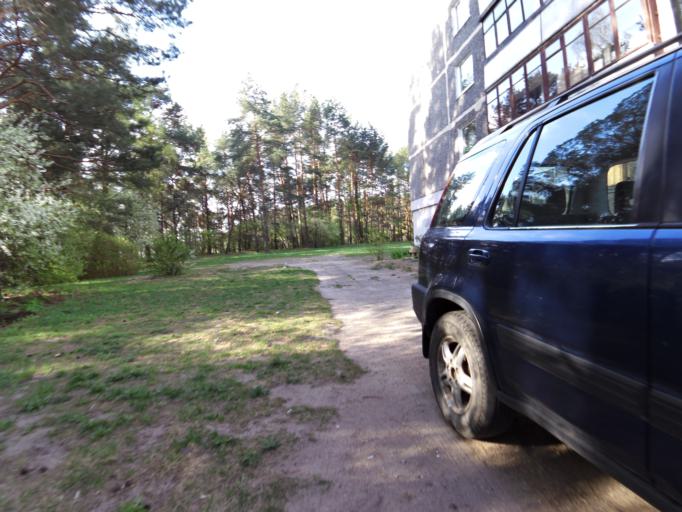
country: LT
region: Vilnius County
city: Lazdynai
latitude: 54.6788
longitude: 25.2200
